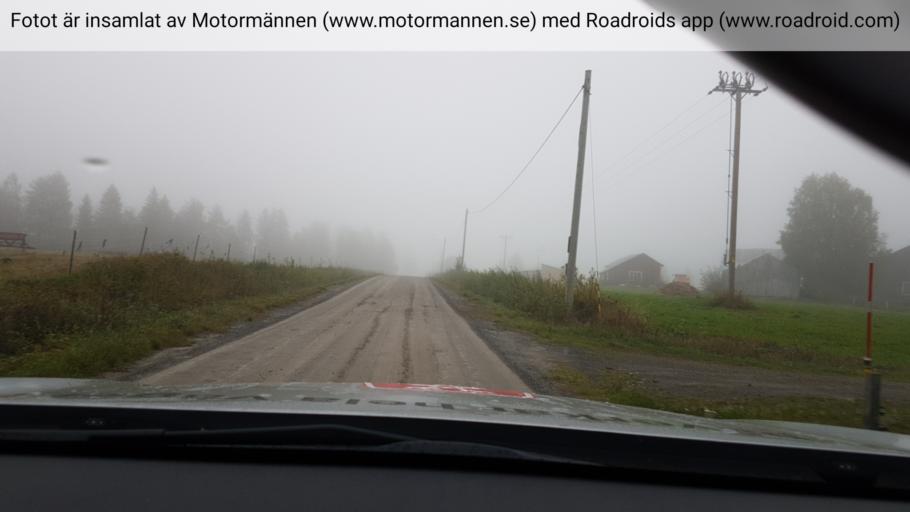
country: SE
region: Vaesterbotten
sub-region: Umea Kommun
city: Ersmark
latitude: 64.1056
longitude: 20.3220
